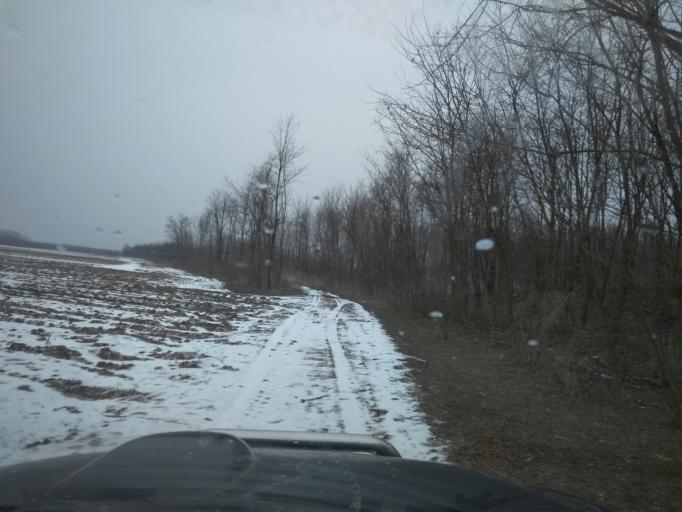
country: HU
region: Szabolcs-Szatmar-Bereg
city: Apagy
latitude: 47.9812
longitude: 21.9114
